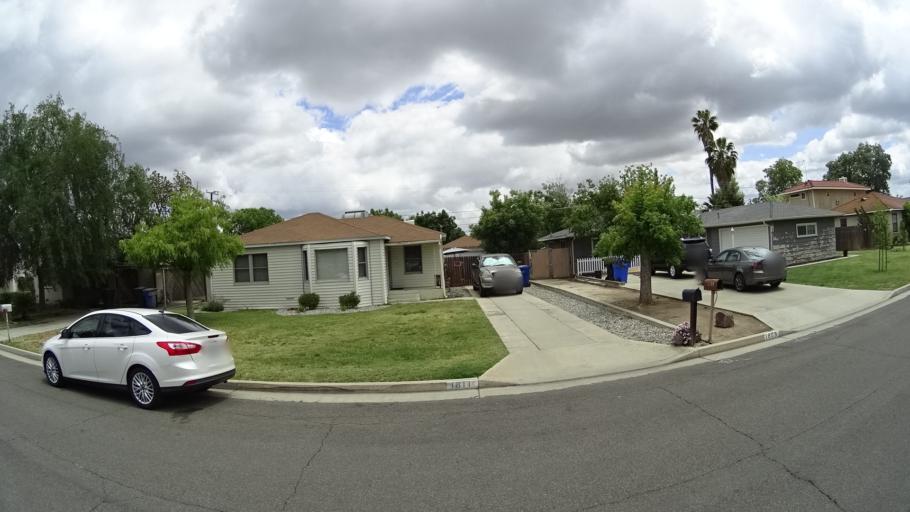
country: US
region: California
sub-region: Kings County
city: Hanford
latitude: 36.3450
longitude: -119.6540
